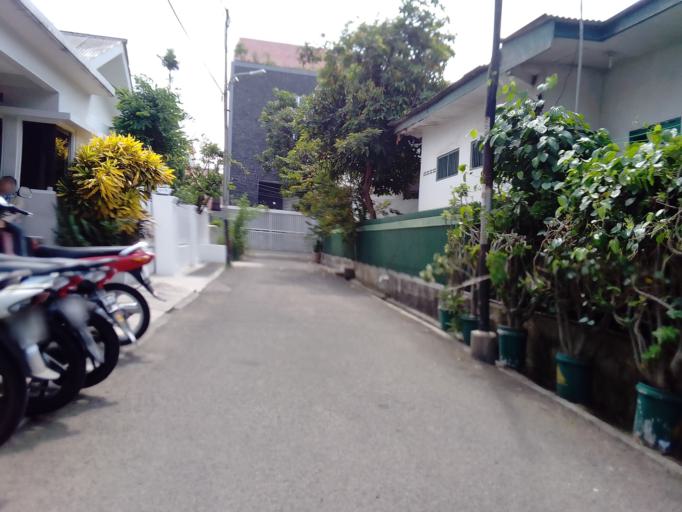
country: ID
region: Jakarta Raya
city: Jakarta
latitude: -6.1754
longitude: 106.8084
